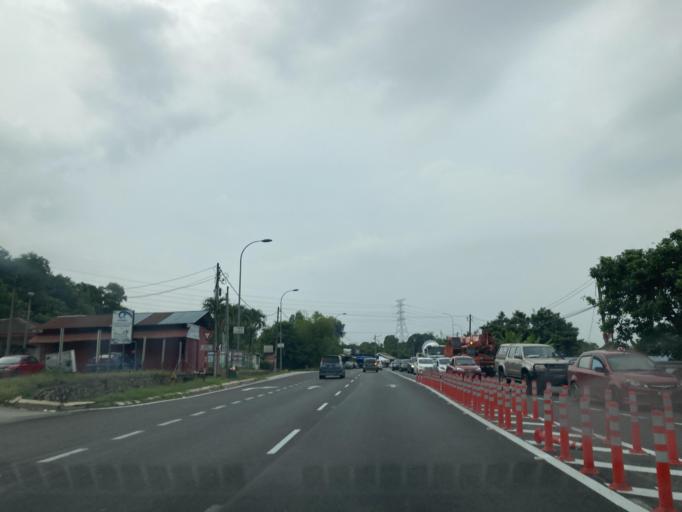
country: MY
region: Selangor
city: Kuang
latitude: 3.2169
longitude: 101.5292
